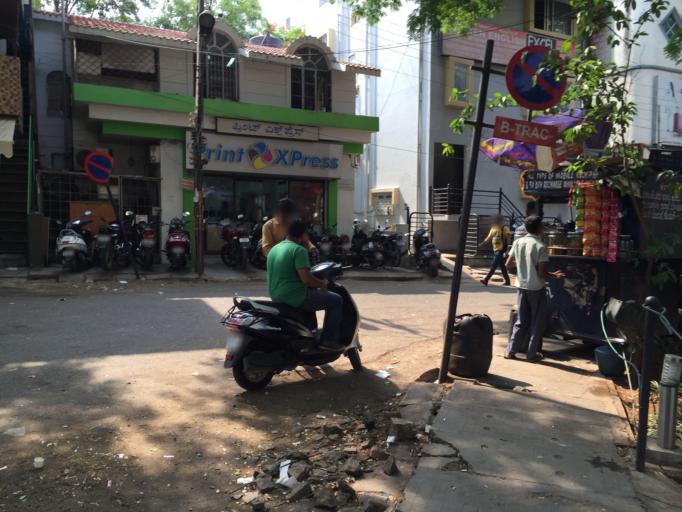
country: IN
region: Karnataka
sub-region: Bangalore Urban
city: Bangalore
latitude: 12.9347
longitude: 77.6129
